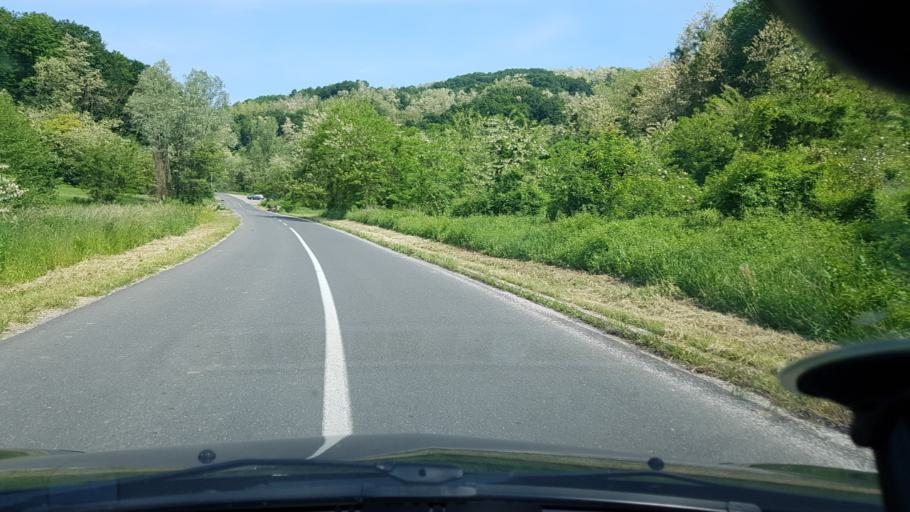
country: HR
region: Krapinsko-Zagorska
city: Marija Bistrica
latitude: 45.9477
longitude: 16.1588
